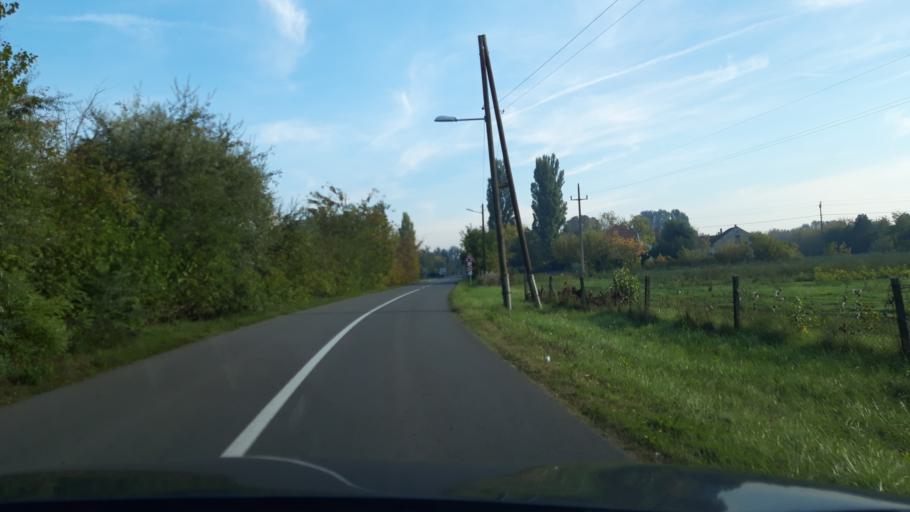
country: HU
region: Csongrad
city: Asotthalom
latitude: 46.1238
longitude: 19.8483
